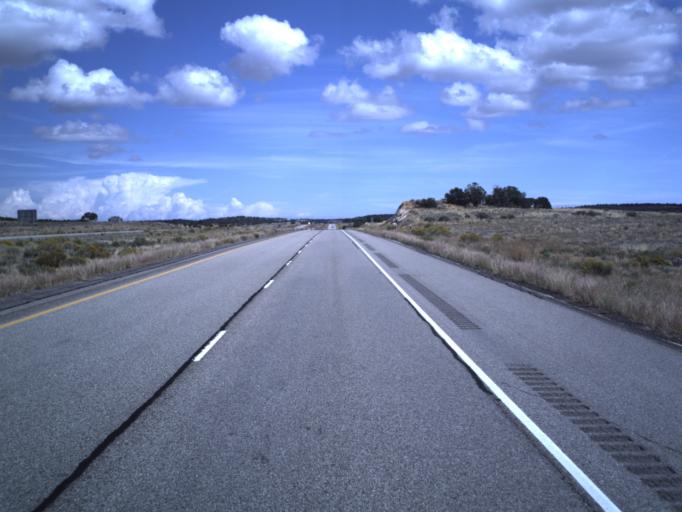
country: US
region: Utah
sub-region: Emery County
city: Castle Dale
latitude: 38.8688
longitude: -110.7756
